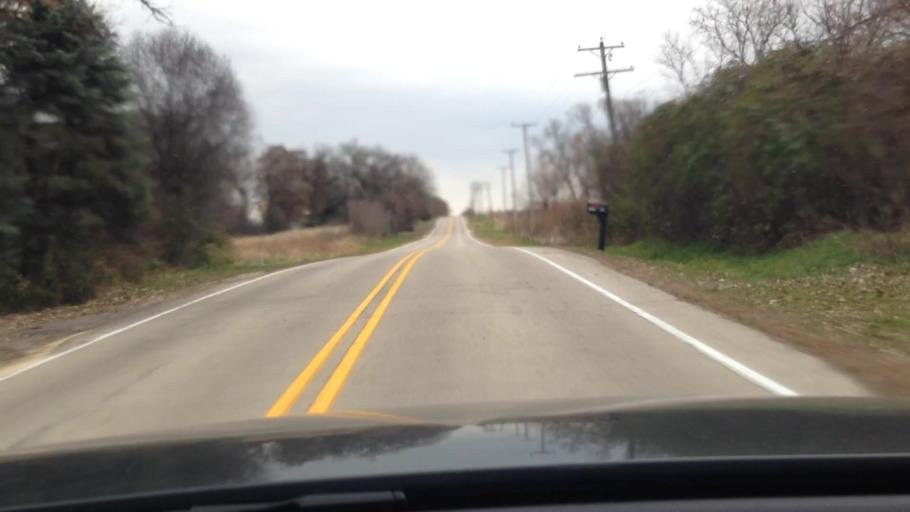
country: US
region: Illinois
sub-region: McHenry County
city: Woodstock
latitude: 42.2767
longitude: -88.4594
